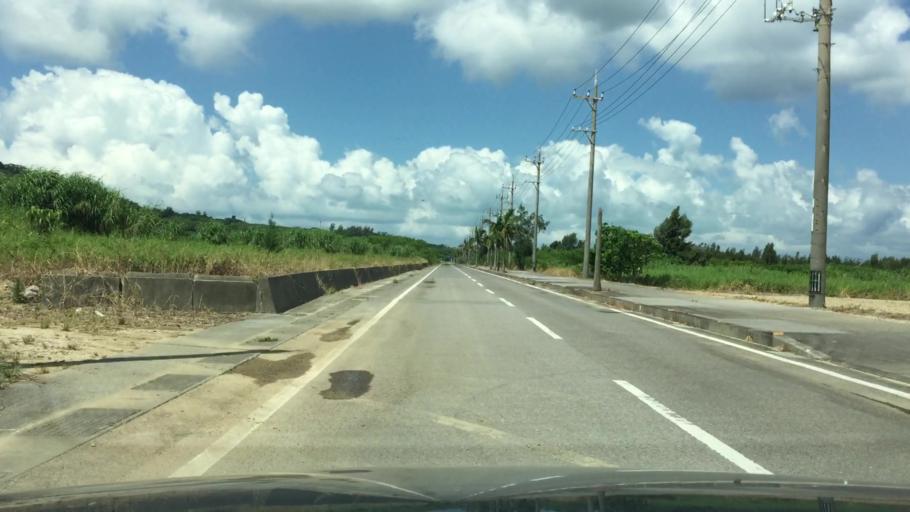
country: JP
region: Okinawa
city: Ishigaki
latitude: 24.3869
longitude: 124.1455
